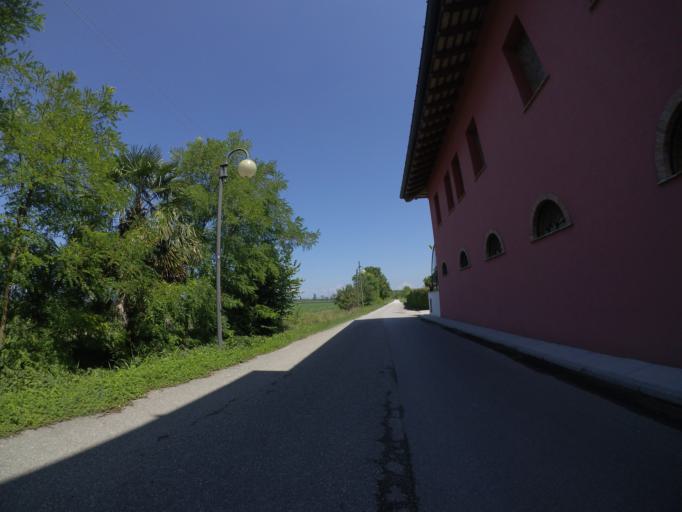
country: IT
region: Friuli Venezia Giulia
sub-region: Provincia di Udine
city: Varmo
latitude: 45.9105
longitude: 13.0066
